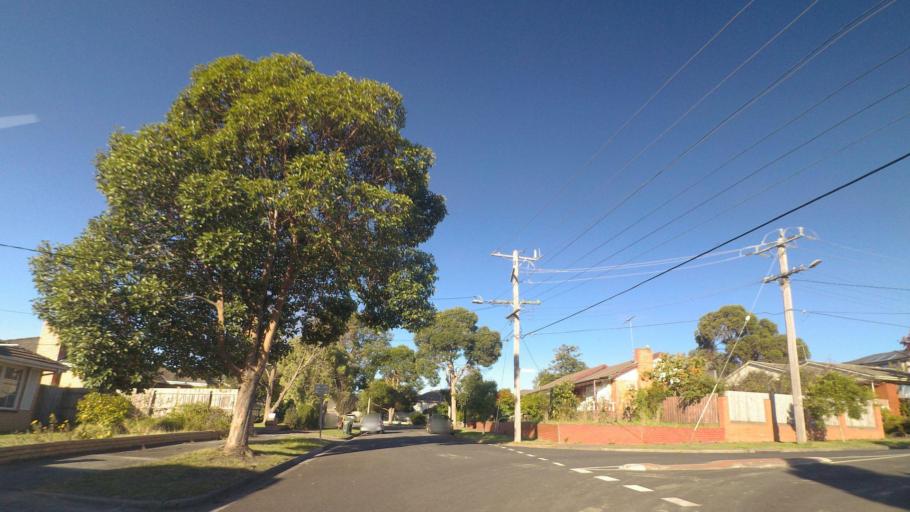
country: AU
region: Victoria
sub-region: Manningham
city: Doncaster East
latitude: -37.7847
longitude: 145.1542
